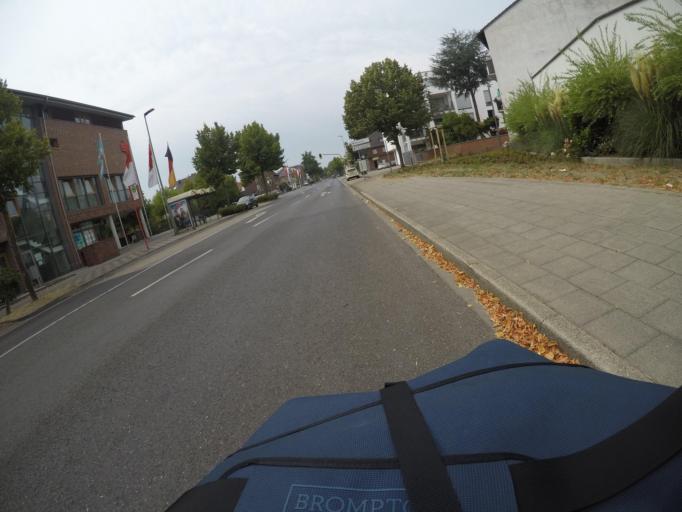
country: DE
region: North Rhine-Westphalia
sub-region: Regierungsbezirk Dusseldorf
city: Dusseldorf
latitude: 51.1774
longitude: 6.7416
